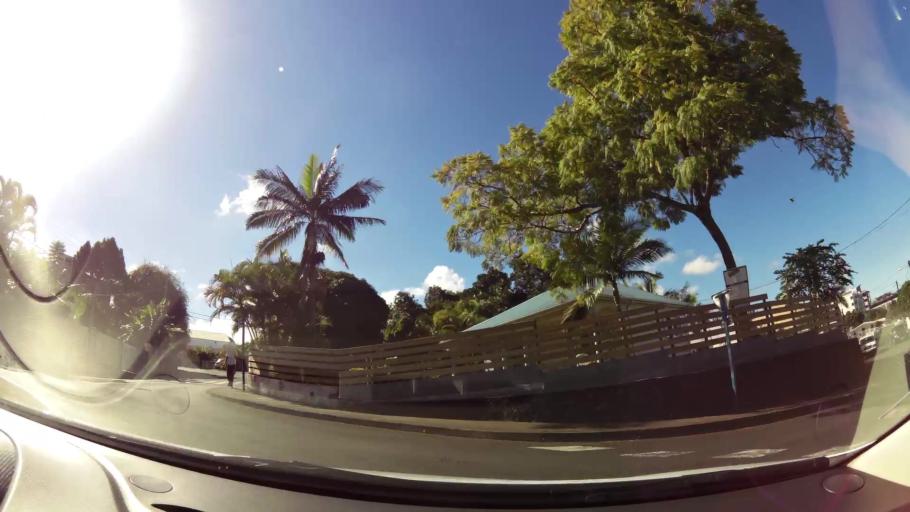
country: RE
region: Reunion
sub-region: Reunion
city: Le Tampon
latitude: -21.2781
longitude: 55.5176
